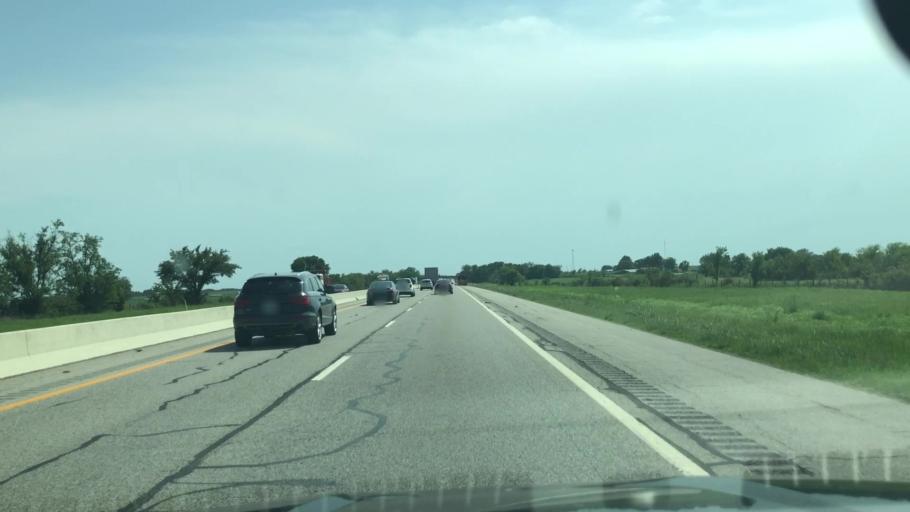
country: US
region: Oklahoma
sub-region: Ottawa County
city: Fairland
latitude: 36.7641
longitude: -94.8976
